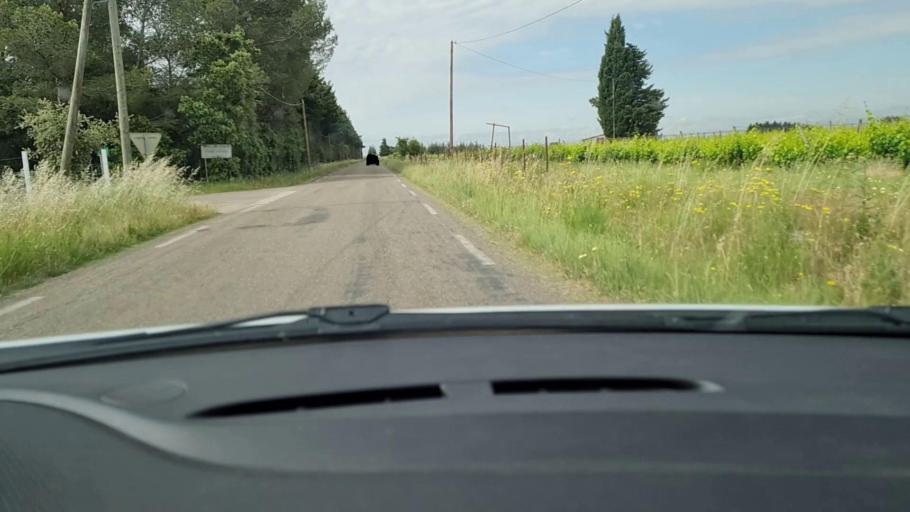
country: FR
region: Languedoc-Roussillon
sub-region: Departement du Gard
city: Bellegarde
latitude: 43.7908
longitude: 4.5294
